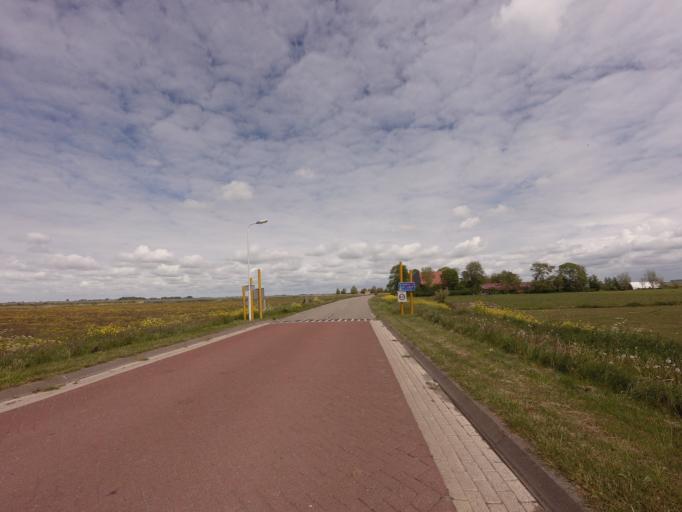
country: NL
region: Friesland
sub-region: Gemeente Gaasterlan-Sleat
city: Balk
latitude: 52.9299
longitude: 5.5452
